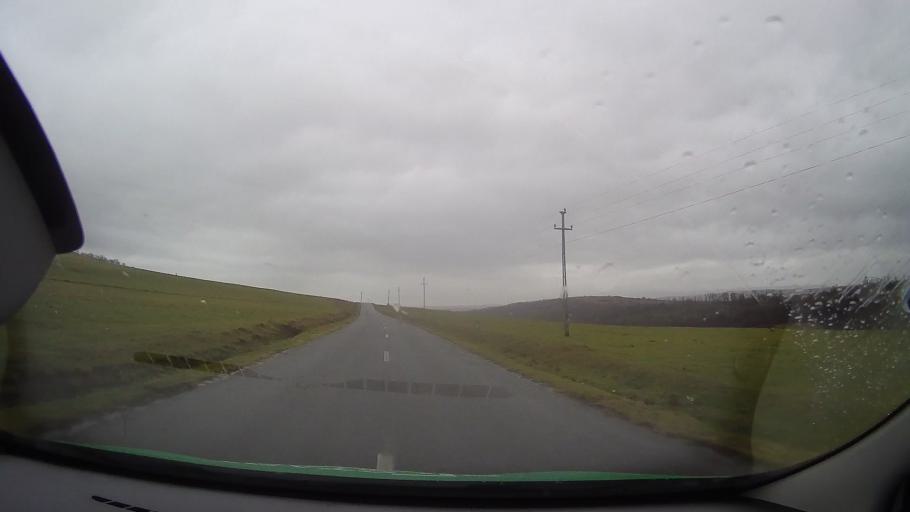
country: RO
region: Mures
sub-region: Comuna Brancovenesti
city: Valenii de Mures
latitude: 46.9127
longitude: 24.7821
